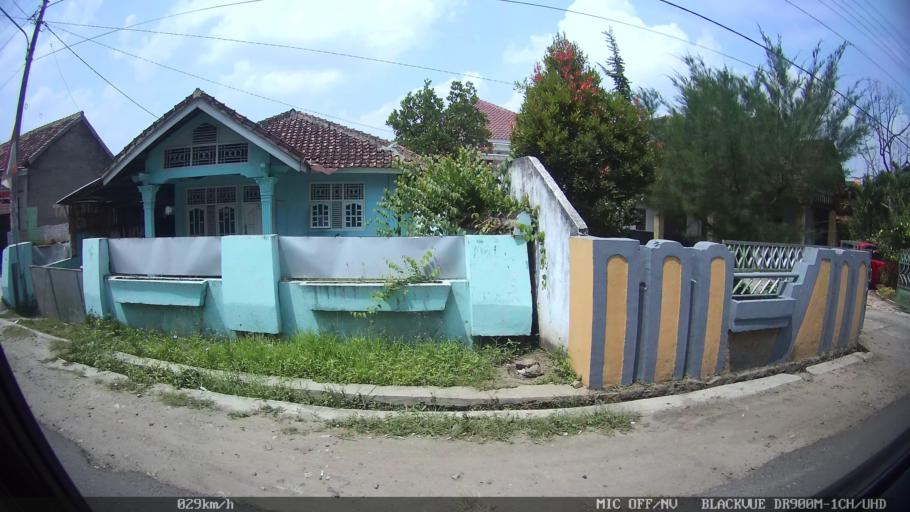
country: ID
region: Lampung
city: Pringsewu
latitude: -5.3539
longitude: 104.9748
